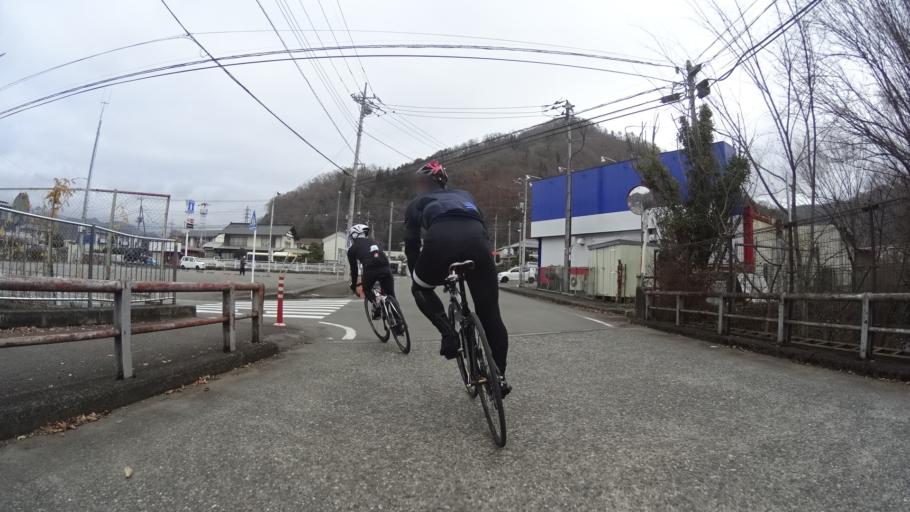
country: JP
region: Yamanashi
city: Otsuki
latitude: 35.5904
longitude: 138.9304
